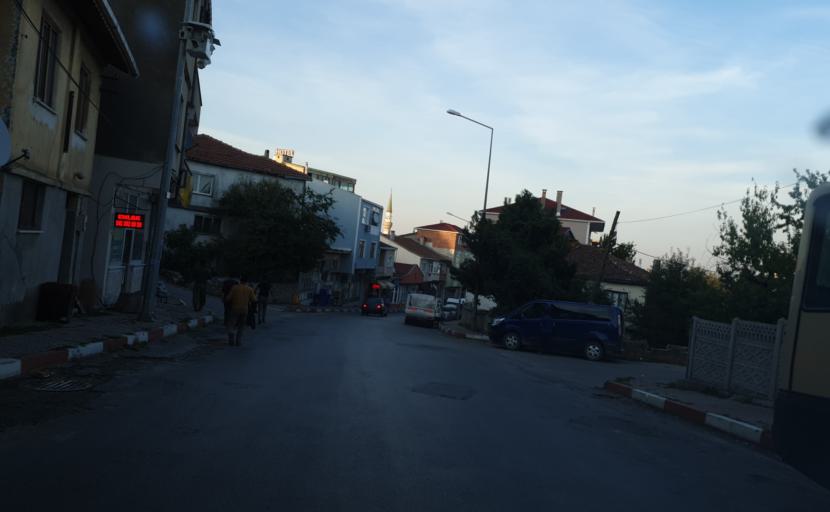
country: TR
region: Kirklareli
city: Sergen
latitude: 41.8239
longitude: 27.7642
